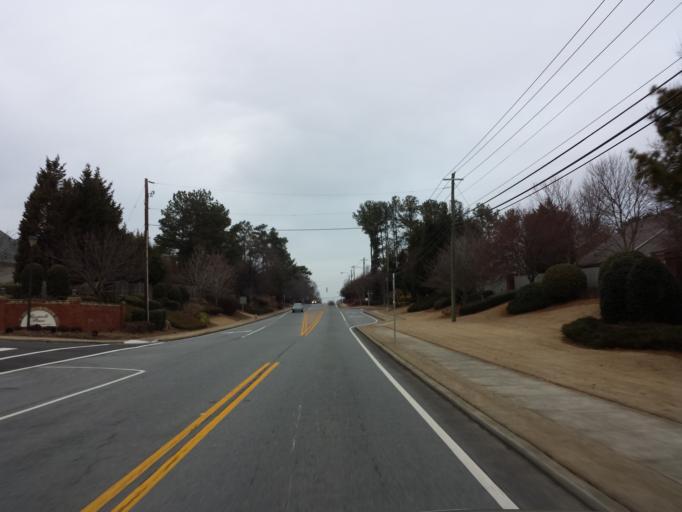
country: US
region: Georgia
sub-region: Fulton County
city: Roswell
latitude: 34.0419
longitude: -84.3613
